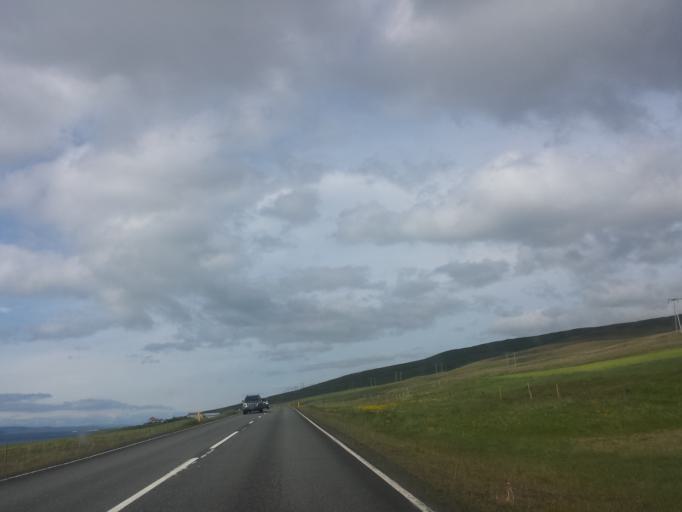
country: IS
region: West
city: Borgarnes
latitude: 65.1934
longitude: -21.0588
